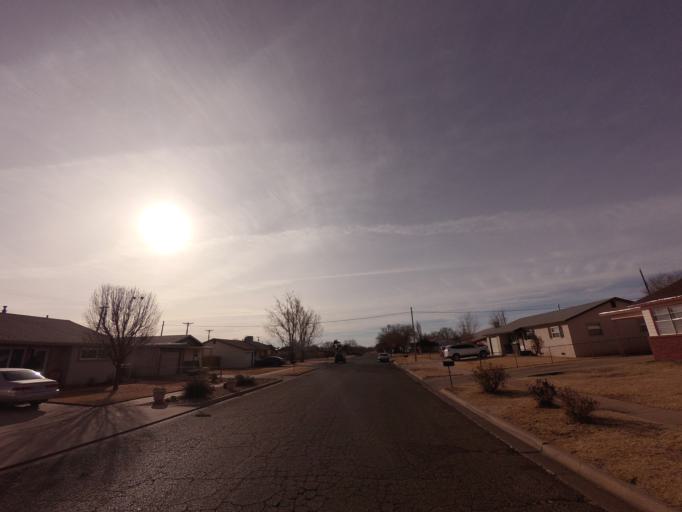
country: US
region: New Mexico
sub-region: Curry County
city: Clovis
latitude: 34.4164
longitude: -103.2191
